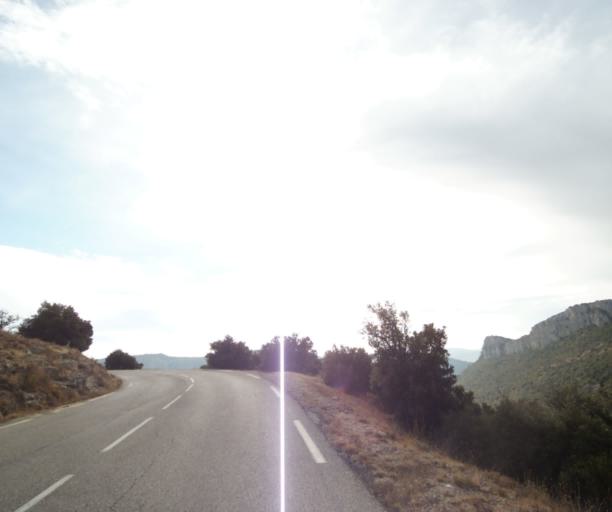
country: FR
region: Provence-Alpes-Cote d'Azur
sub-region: Departement des Bouches-du-Rhone
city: Gemenos
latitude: 43.3161
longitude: 5.6653
